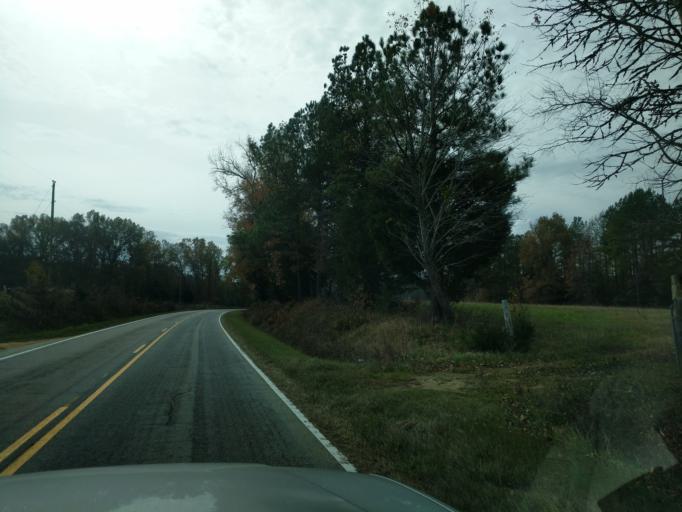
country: US
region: South Carolina
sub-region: Laurens County
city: Joanna
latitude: 34.2919
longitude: -81.8447
